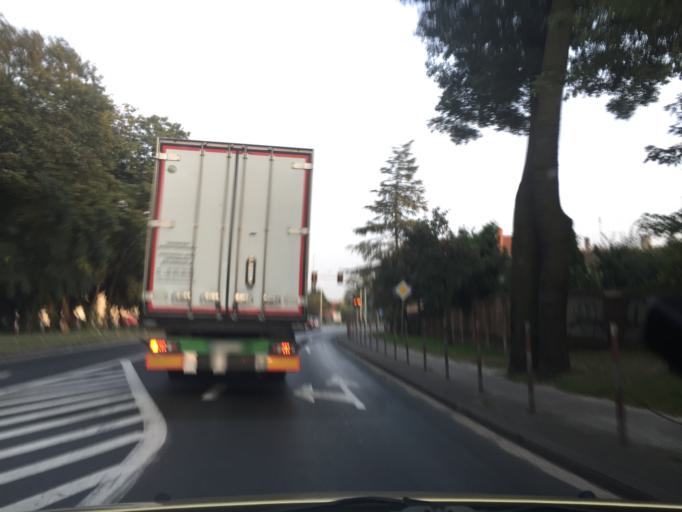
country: PL
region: Greater Poland Voivodeship
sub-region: Powiat jarocinski
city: Jarocin
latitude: 51.9734
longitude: 17.5023
